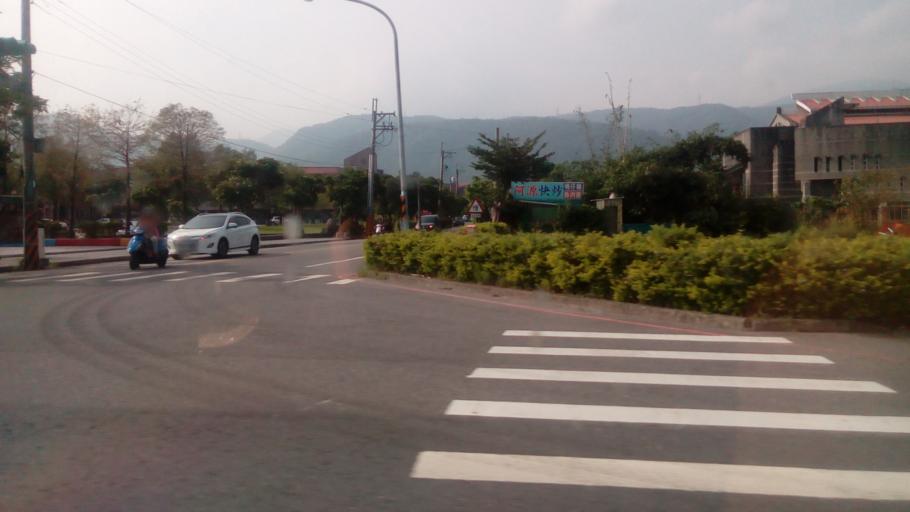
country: TW
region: Taiwan
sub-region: Yilan
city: Yilan
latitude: 24.6332
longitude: 121.7914
